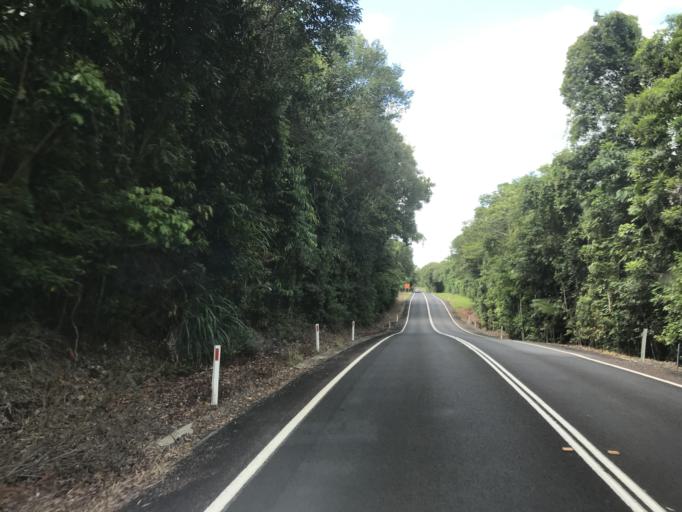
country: AU
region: Queensland
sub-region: Cassowary Coast
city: Innisfail
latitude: -17.8567
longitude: 146.0656
